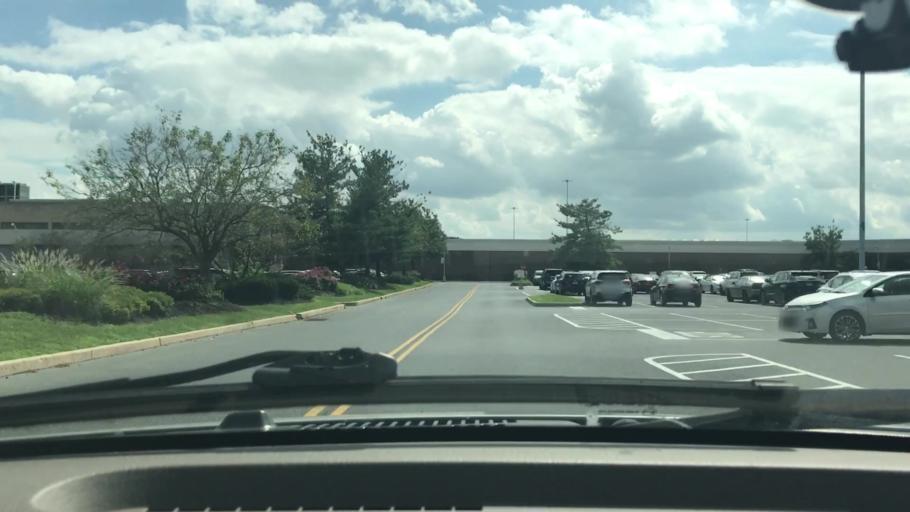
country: US
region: Pennsylvania
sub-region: Lancaster County
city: East Petersburg
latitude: 40.0686
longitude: -76.3372
